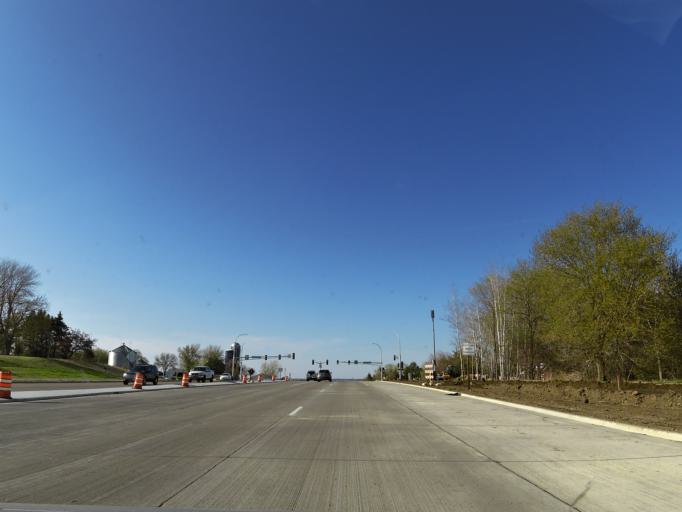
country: US
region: Minnesota
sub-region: Scott County
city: Shakopee
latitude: 44.7598
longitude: -93.5052
